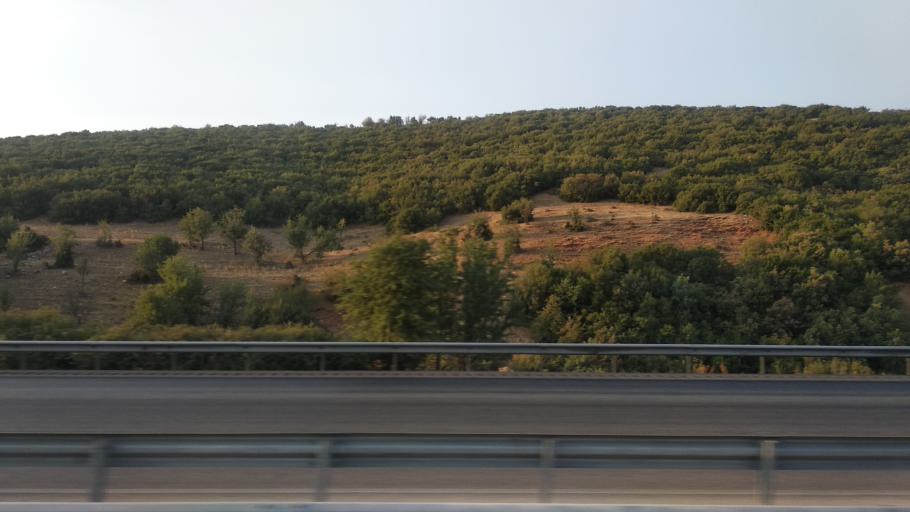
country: TR
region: Manisa
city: Menye
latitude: 38.5537
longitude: 28.4727
